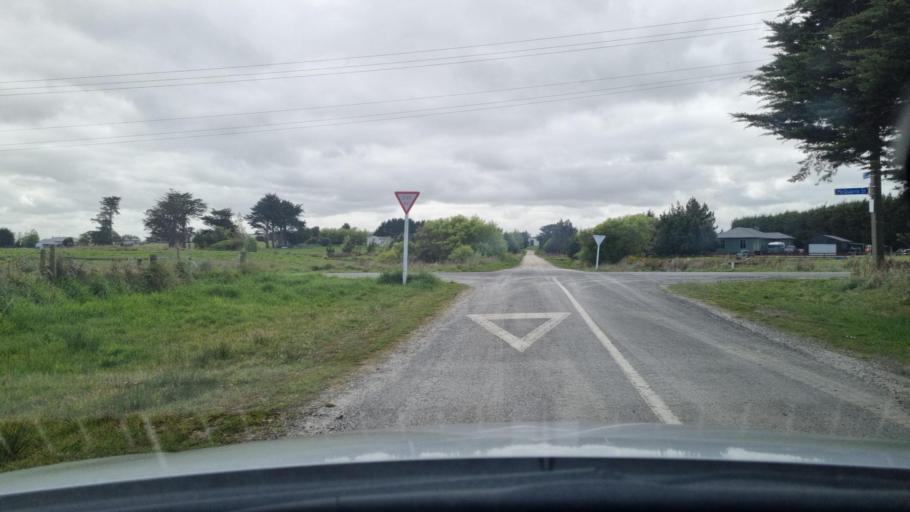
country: NZ
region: Southland
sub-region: Invercargill City
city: Invercargill
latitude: -46.4361
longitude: 168.3897
